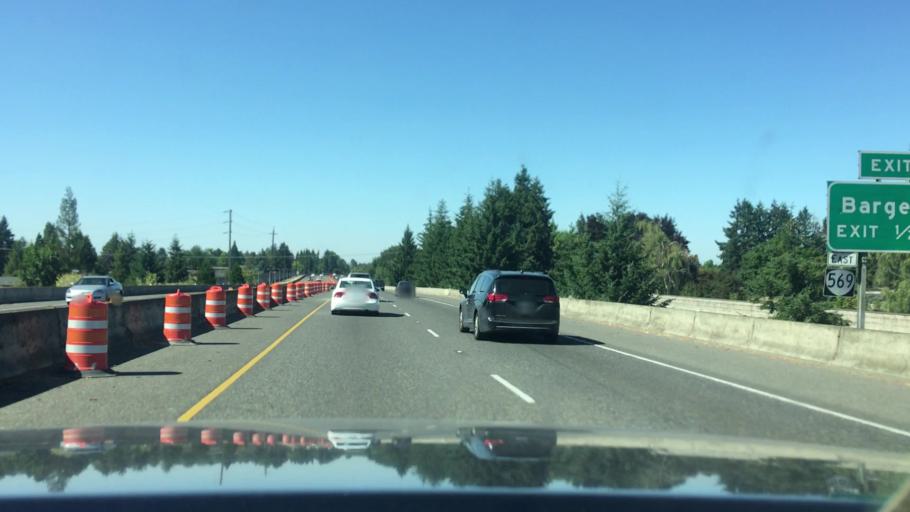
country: US
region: Oregon
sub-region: Lane County
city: Eugene
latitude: 44.0715
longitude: -123.1736
